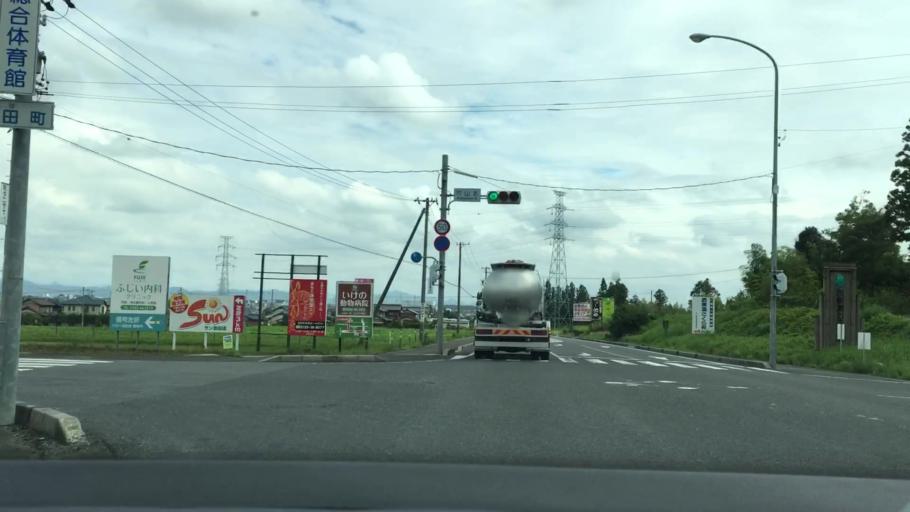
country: JP
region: Gifu
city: Godo
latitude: 35.4206
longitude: 136.5635
